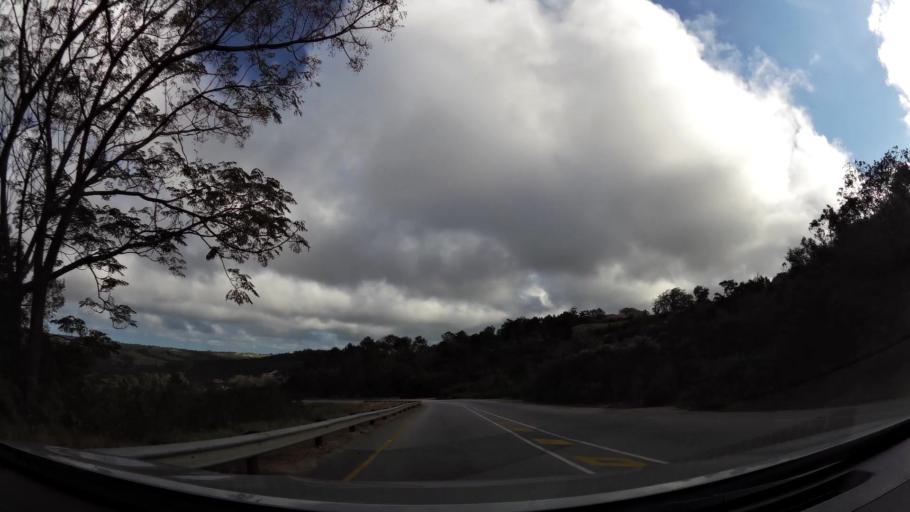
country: ZA
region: Western Cape
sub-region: Eden District Municipality
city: Plettenberg Bay
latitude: -34.0533
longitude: 23.3531
